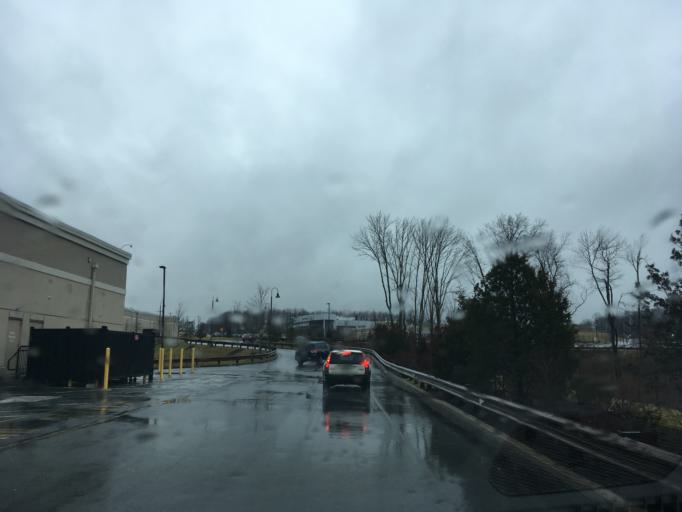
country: US
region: Pennsylvania
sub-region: Delaware County
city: Chester Heights
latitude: 39.8748
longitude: -75.5436
